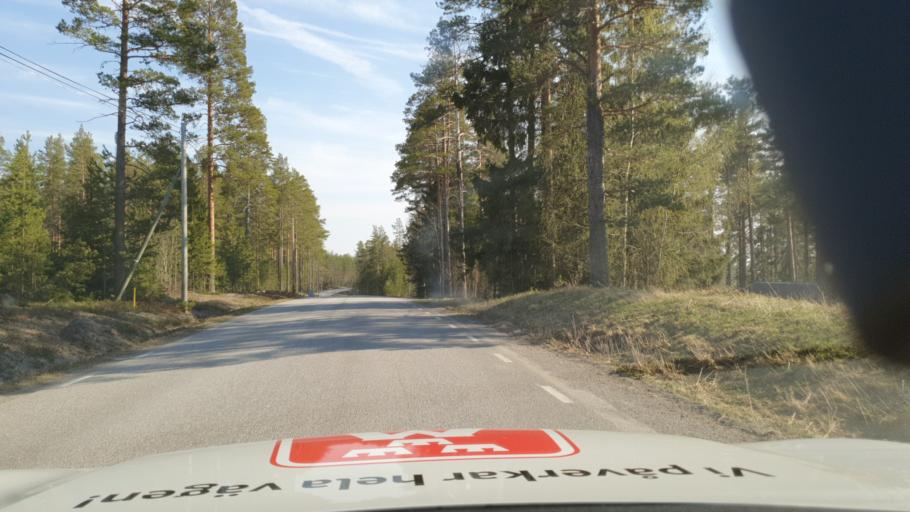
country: SE
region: Vaesterbotten
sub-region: Umea Kommun
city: Roback
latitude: 63.9036
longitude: 20.1532
